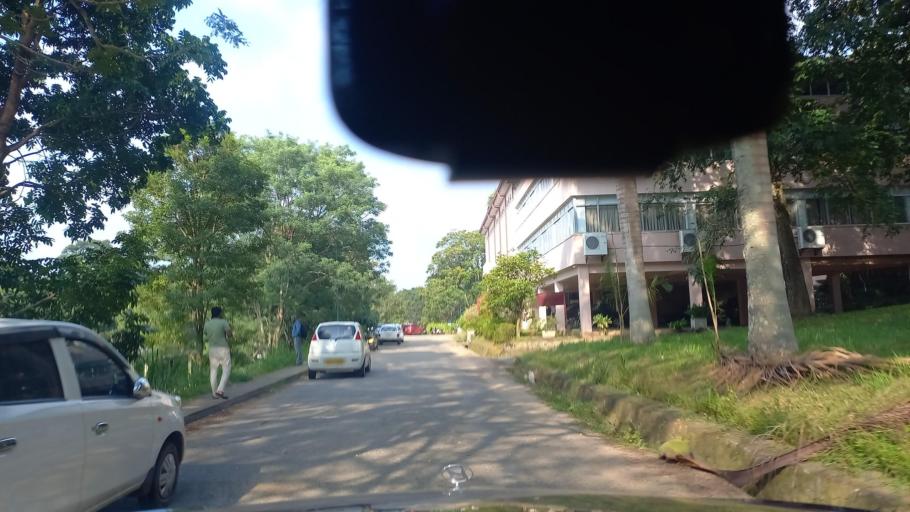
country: LK
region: Central
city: Kandy
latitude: 7.2585
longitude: 80.5973
